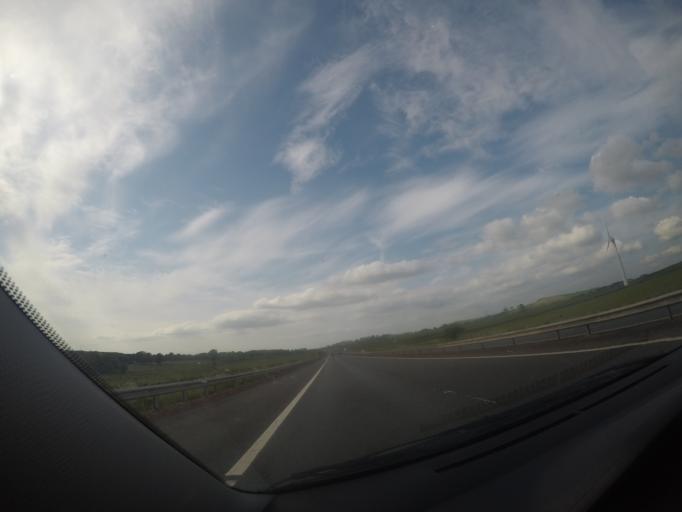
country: GB
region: Scotland
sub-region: South Lanarkshire
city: Lesmahagow
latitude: 55.6181
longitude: -3.8522
